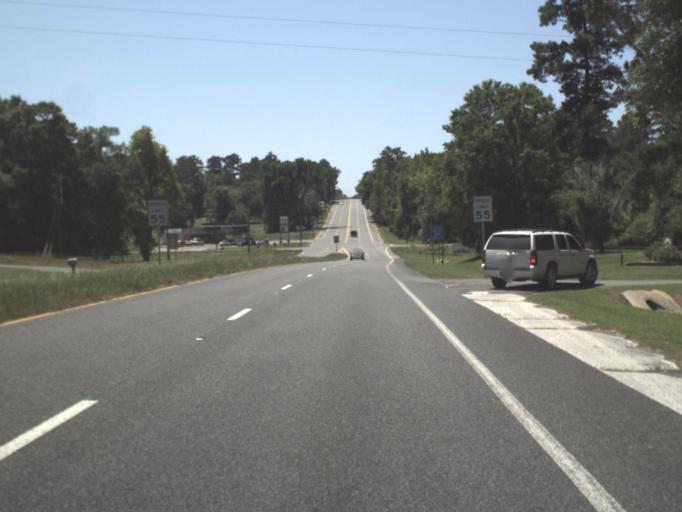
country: US
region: Florida
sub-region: Jefferson County
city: Monticello
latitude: 30.5639
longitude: -83.8702
